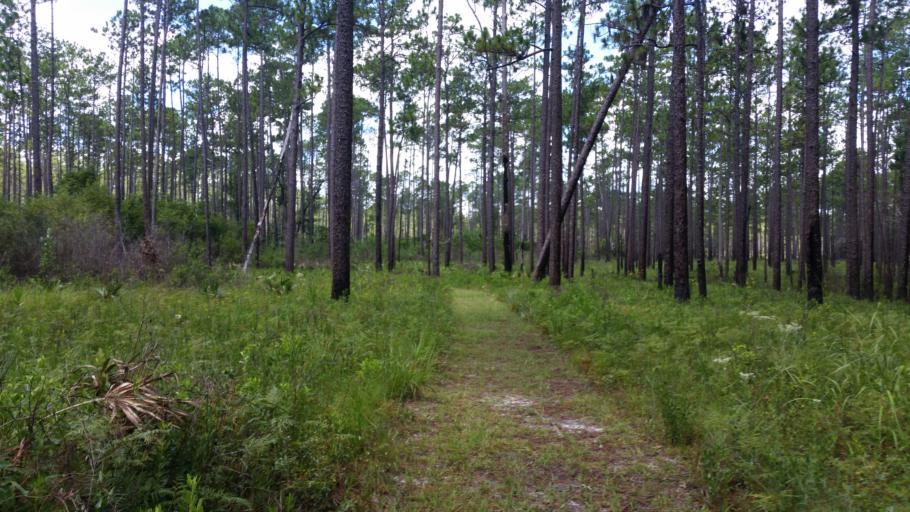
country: US
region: Florida
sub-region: Santa Rosa County
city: East Milton
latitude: 30.7054
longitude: -86.8739
